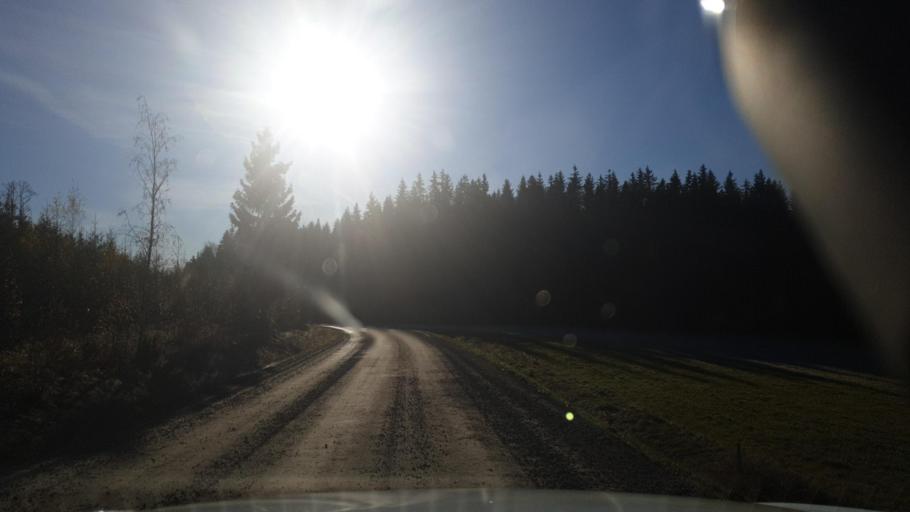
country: SE
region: Vaermland
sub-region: Karlstads Kommun
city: Edsvalla
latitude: 59.4892
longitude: 13.0332
